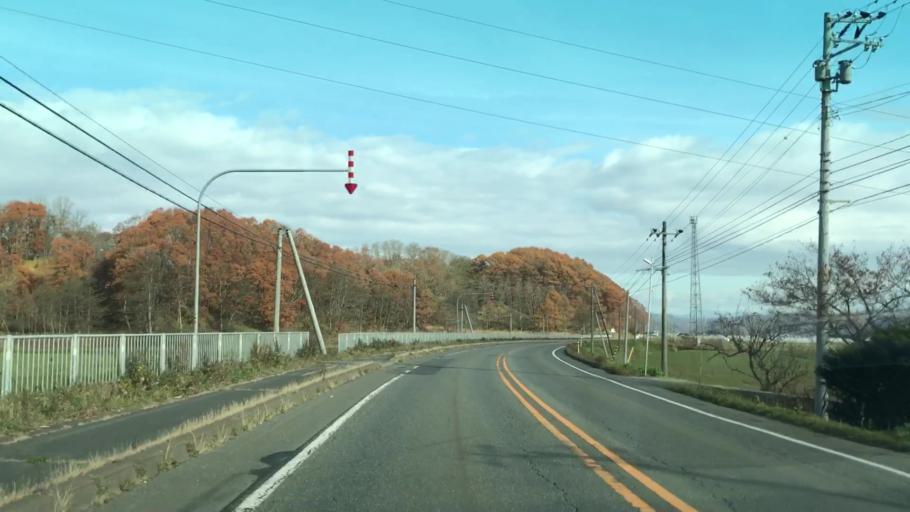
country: JP
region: Hokkaido
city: Shizunai-furukawacho
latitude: 42.5594
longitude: 142.0816
